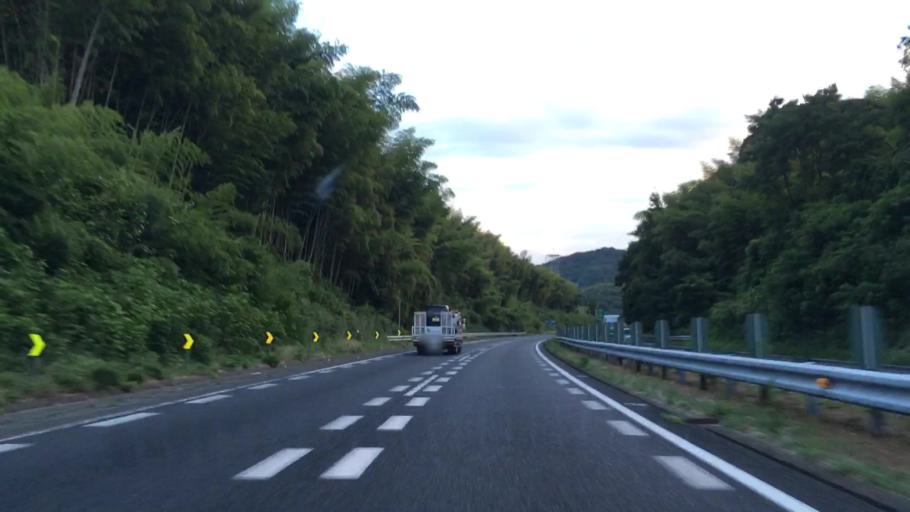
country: JP
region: Yamaguchi
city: Shimonoseki
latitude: 33.9348
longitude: 130.9962
